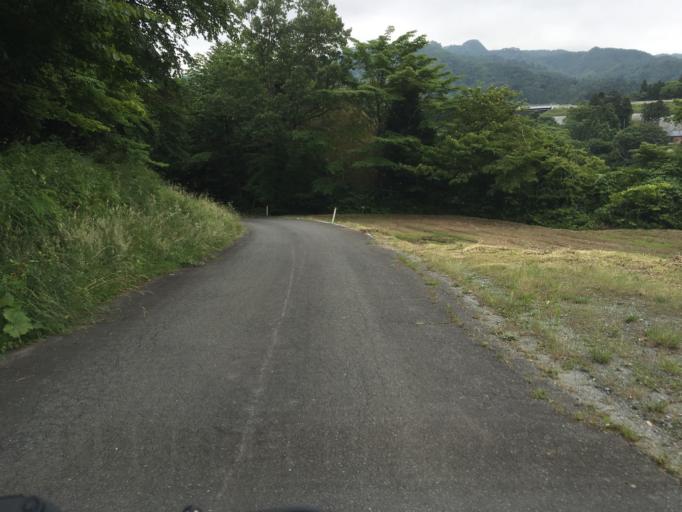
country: JP
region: Miyagi
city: Marumori
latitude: 37.7745
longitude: 140.8313
